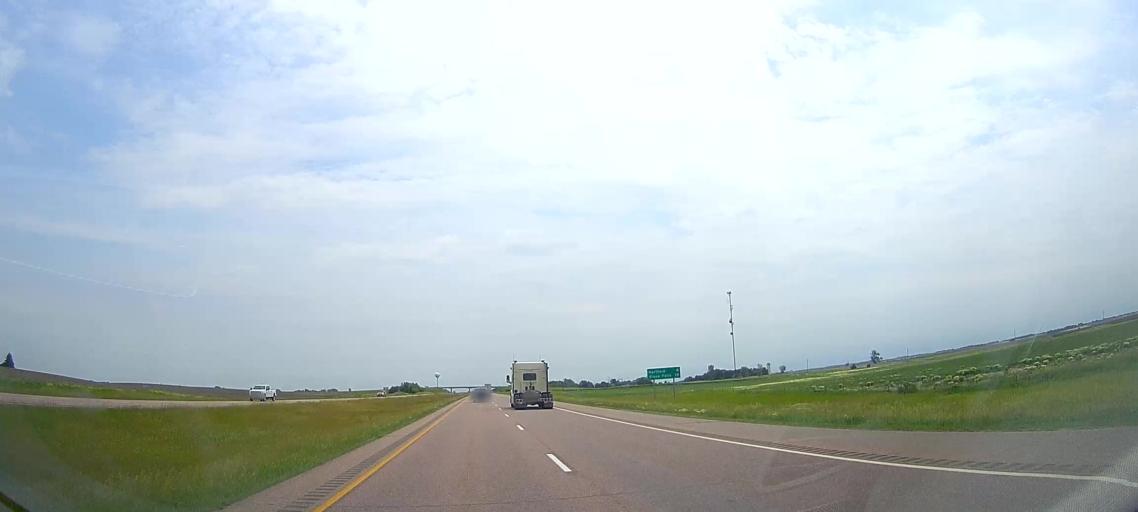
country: US
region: South Dakota
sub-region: Minnehaha County
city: Hartford
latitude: 43.6365
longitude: -97.0774
